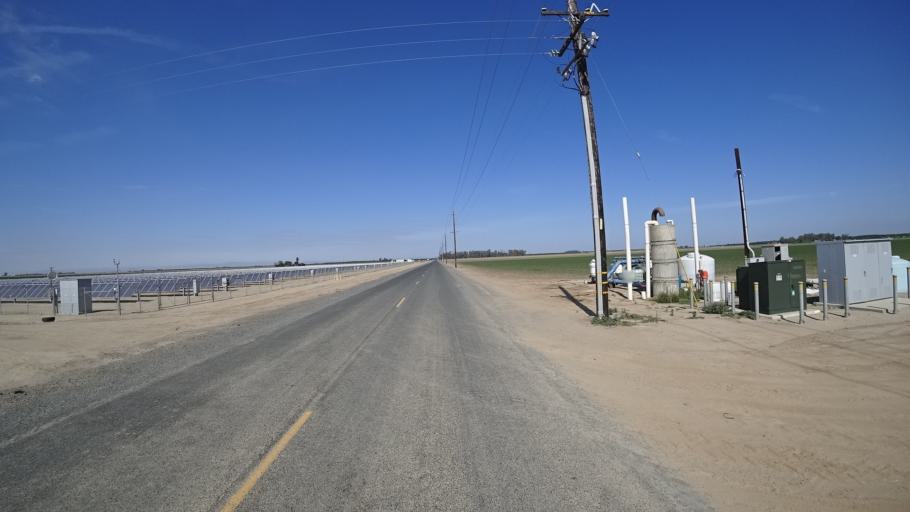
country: US
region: California
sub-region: Kings County
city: Home Garden
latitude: 36.2548
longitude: -119.6636
